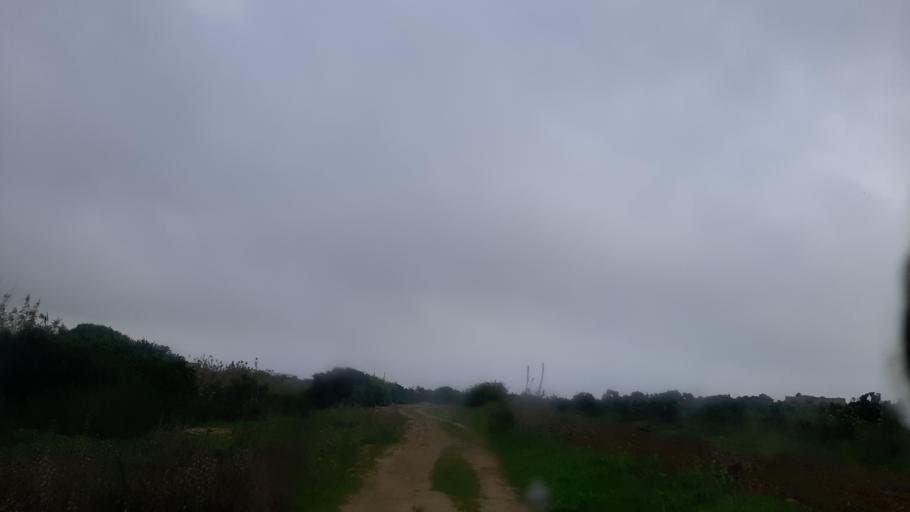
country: TN
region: Nabul
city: Qulaybiyah
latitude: 36.8246
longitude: 11.0429
